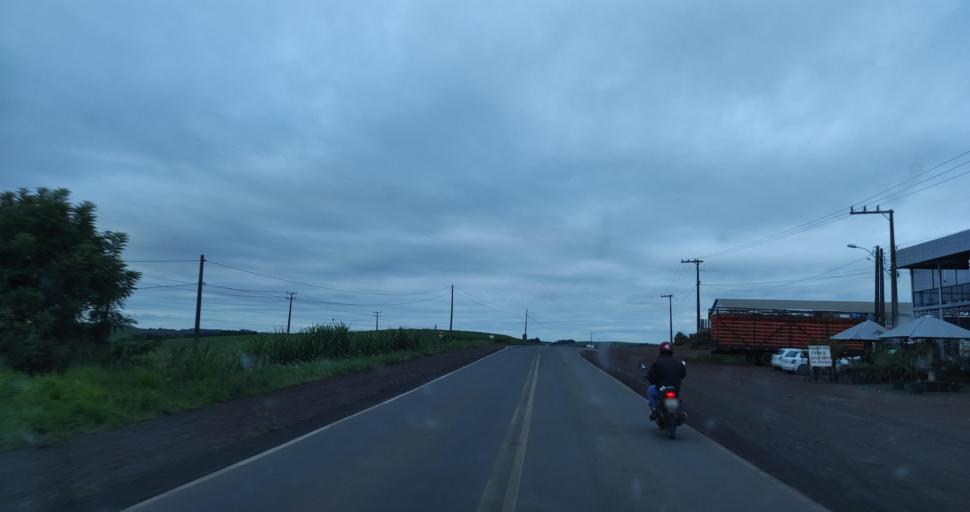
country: BR
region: Santa Catarina
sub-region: Xanxere
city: Xanxere
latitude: -26.7431
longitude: -52.3962
